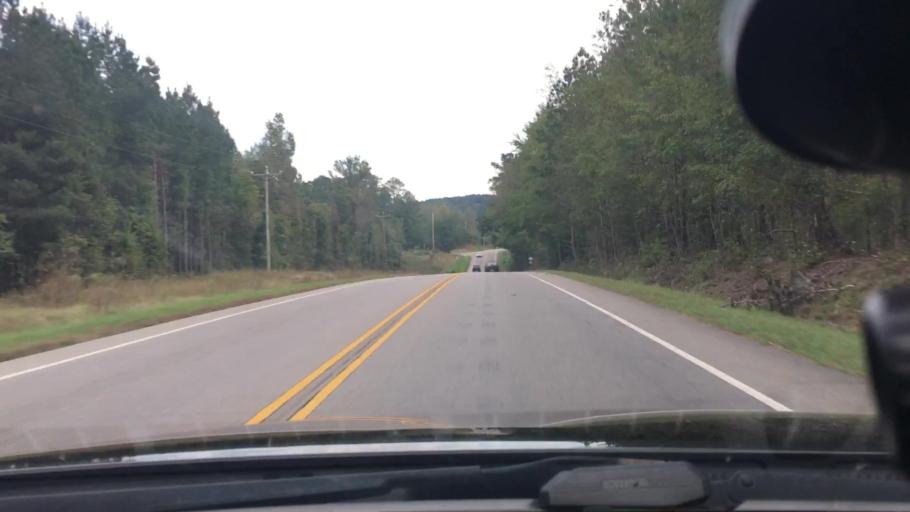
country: US
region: North Carolina
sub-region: Moore County
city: Carthage
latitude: 35.3847
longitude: -79.4912
